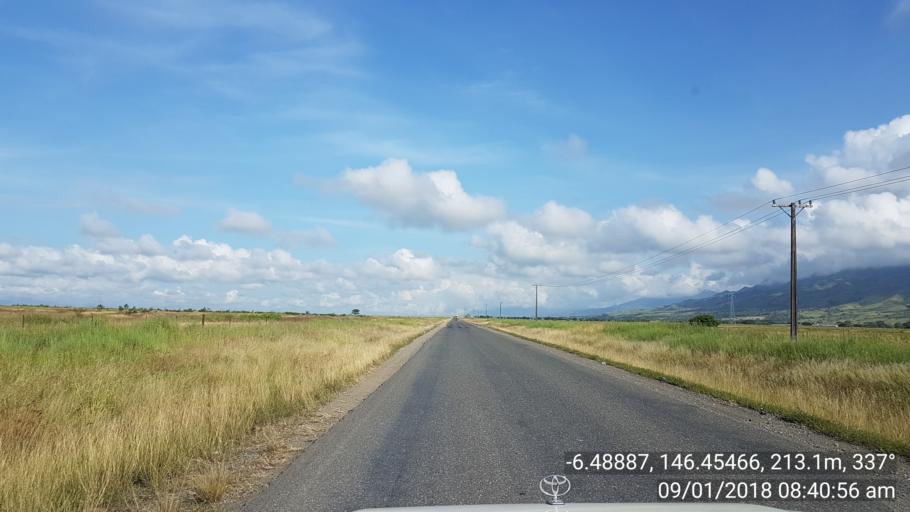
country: PG
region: Morobe
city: Lae
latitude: -6.4891
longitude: 146.4546
